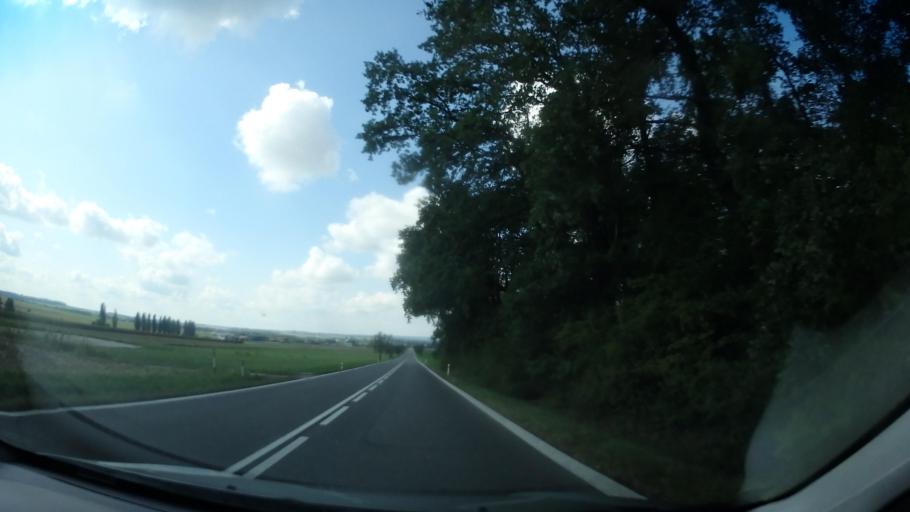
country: CZ
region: Central Bohemia
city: Suchdol
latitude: 49.9565
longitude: 15.1160
